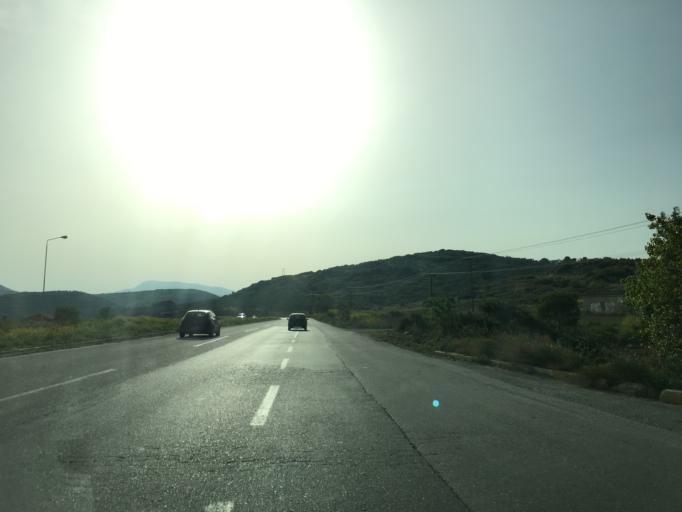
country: GR
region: Thessaly
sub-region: Nomos Magnisias
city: Velestino
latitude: 39.3839
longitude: 22.8388
